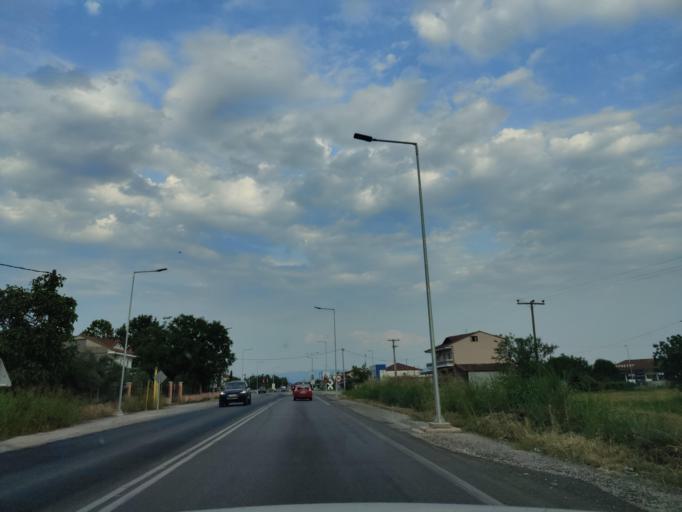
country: GR
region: East Macedonia and Thrace
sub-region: Nomos Dramas
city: Xiropotamos
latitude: 41.1573
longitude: 24.1013
